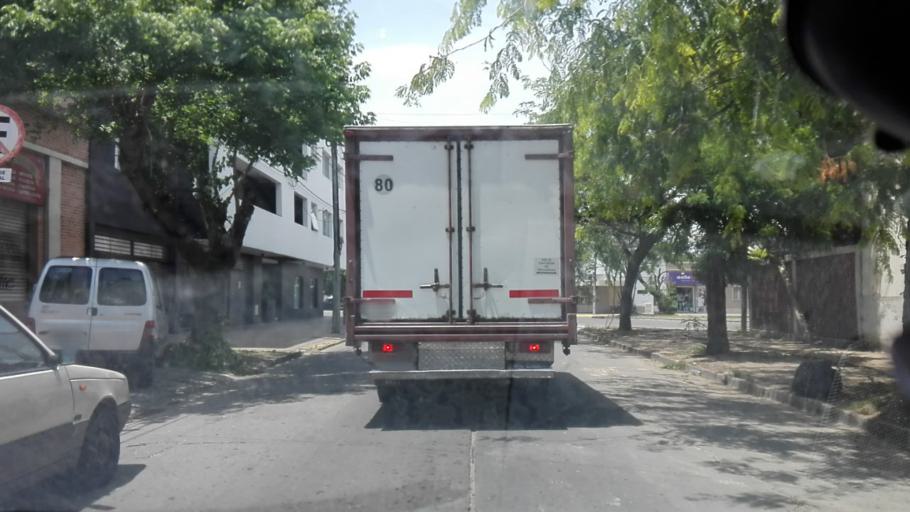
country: AR
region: Buenos Aires
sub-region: Partido de La Plata
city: La Plata
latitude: -34.9217
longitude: -57.9703
